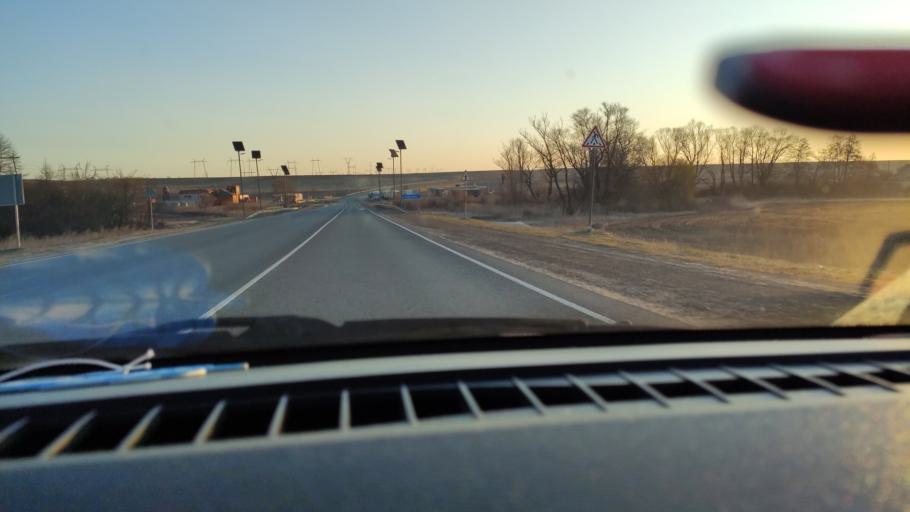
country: RU
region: Saratov
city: Sinodskoye
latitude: 51.9206
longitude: 46.5608
